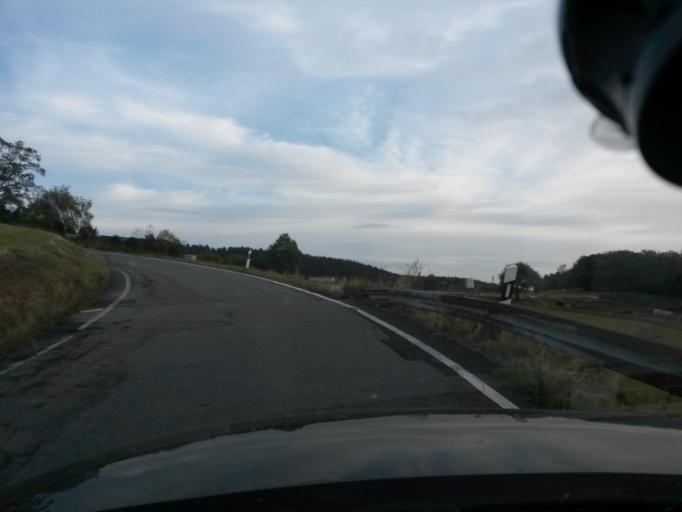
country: DE
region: North Rhine-Westphalia
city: Altena
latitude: 51.2388
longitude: 7.6935
